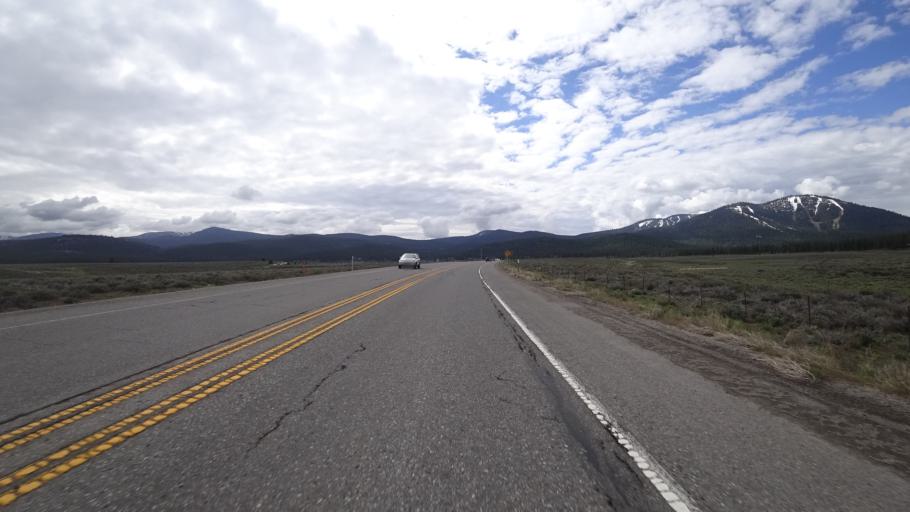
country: US
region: California
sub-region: Nevada County
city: Truckee
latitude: 39.3104
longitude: -120.1391
